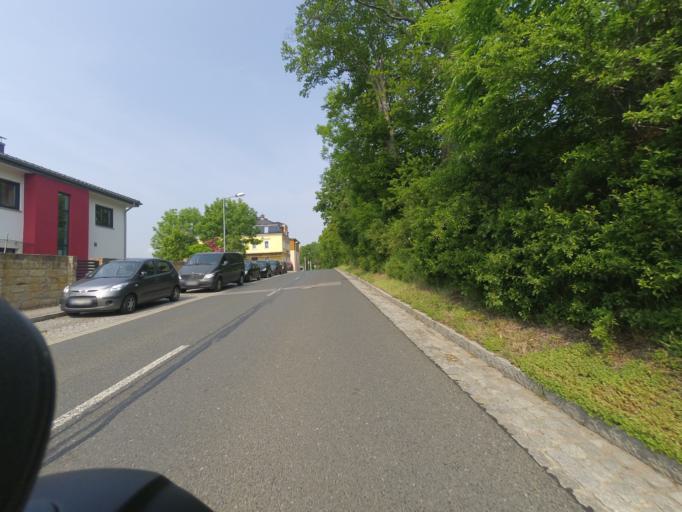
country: DE
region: Saxony
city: Rabenau
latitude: 50.9660
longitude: 13.6372
